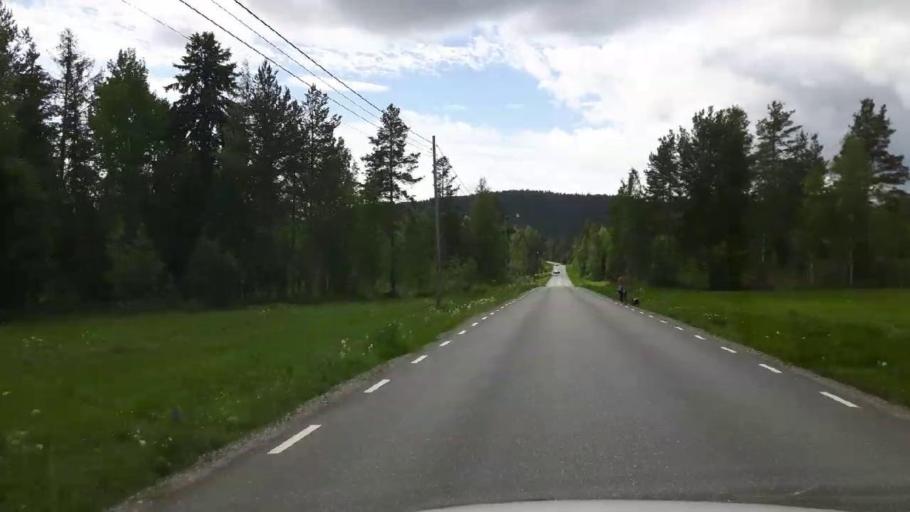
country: SE
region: Dalarna
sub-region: Faluns Kommun
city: Falun
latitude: 60.6766
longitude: 15.7561
